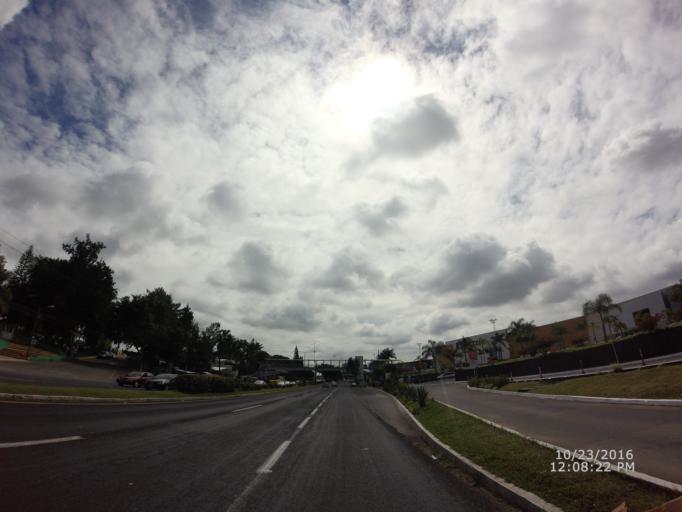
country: MX
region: Veracruz
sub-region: Xalapa
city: Colonia Santa Barbara
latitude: 19.5137
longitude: -96.8761
